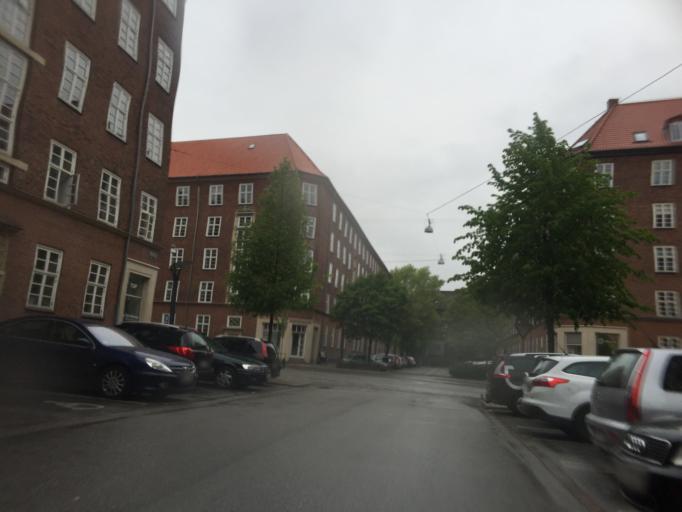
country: DK
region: Capital Region
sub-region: Frederiksberg Kommune
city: Frederiksberg
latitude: 55.6827
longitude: 12.5122
